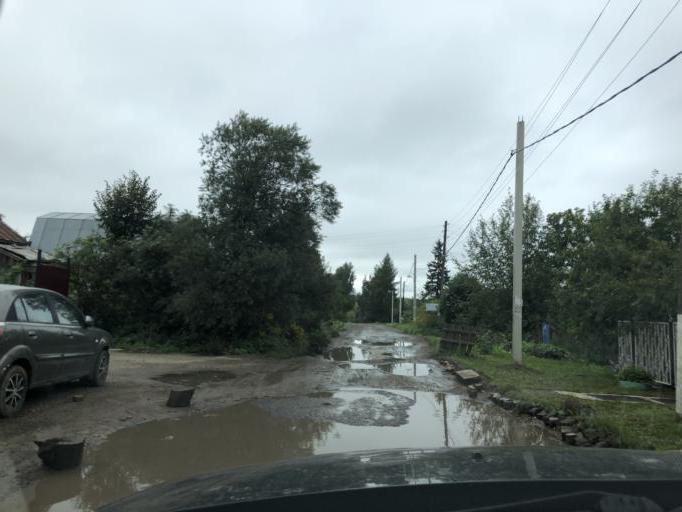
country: RU
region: Tula
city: Mendeleyevskiy
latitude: 54.1653
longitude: 37.5504
